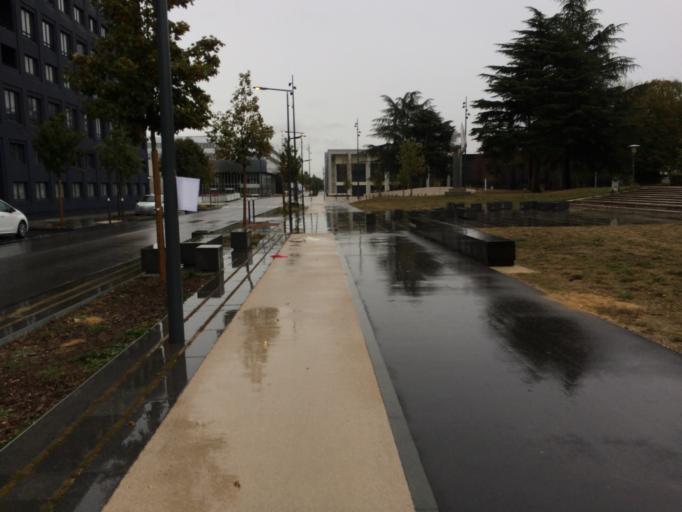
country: FR
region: Ile-de-France
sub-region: Departement de l'Essonne
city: Bures-sur-Yvette
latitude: 48.7097
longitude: 2.1637
